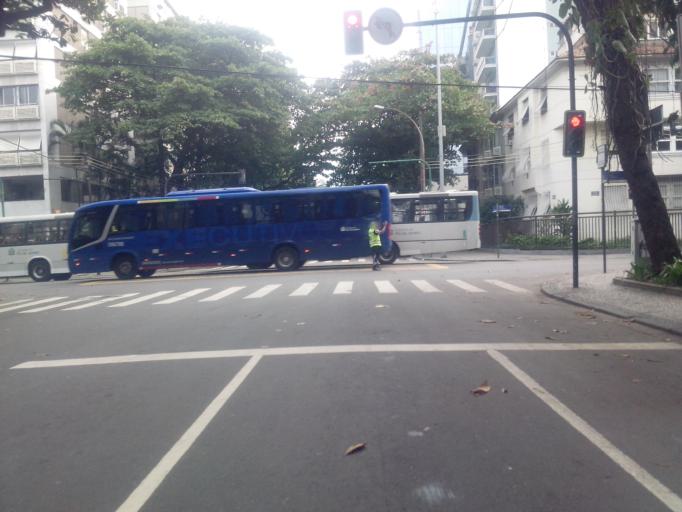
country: BR
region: Rio de Janeiro
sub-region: Rio De Janeiro
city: Rio de Janeiro
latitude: -22.9851
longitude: -43.2175
